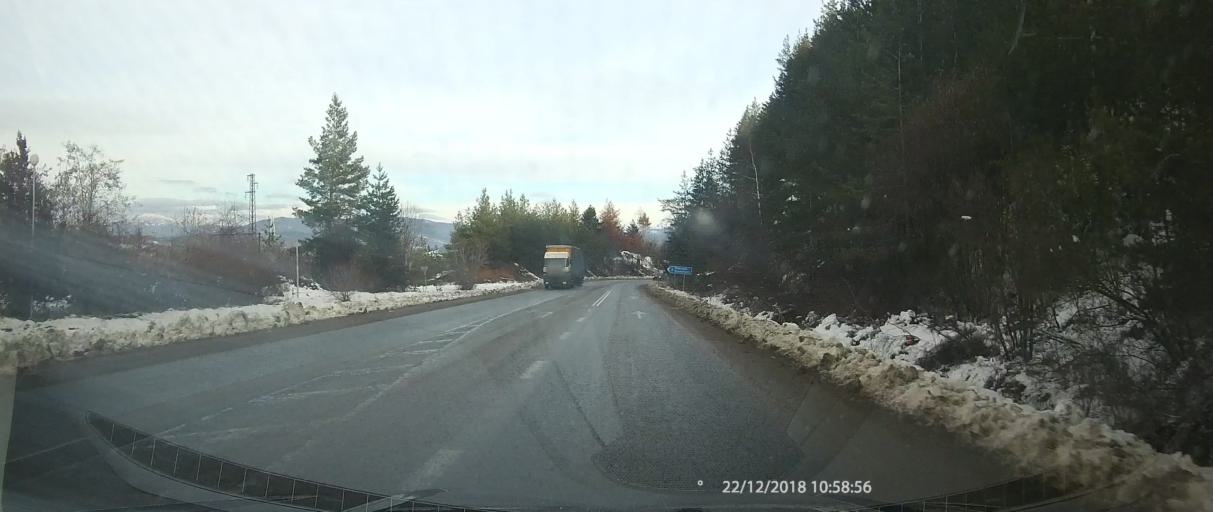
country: MK
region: Kriva Palanka
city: Kriva Palanka
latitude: 42.2225
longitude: 22.4745
